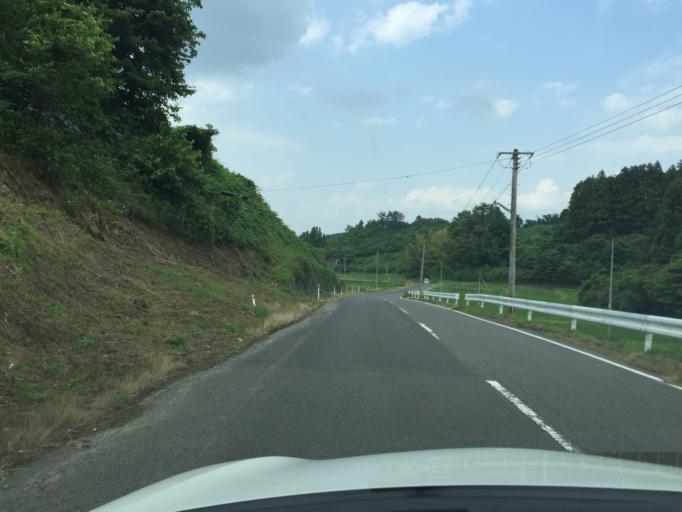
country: JP
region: Fukushima
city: Miharu
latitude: 37.3702
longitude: 140.4894
